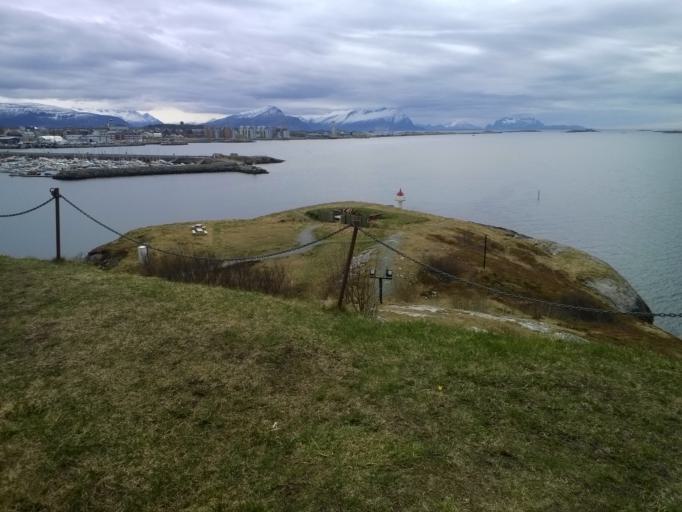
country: NO
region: Nordland
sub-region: Bodo
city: Bodo
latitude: 67.2875
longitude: 14.3670
